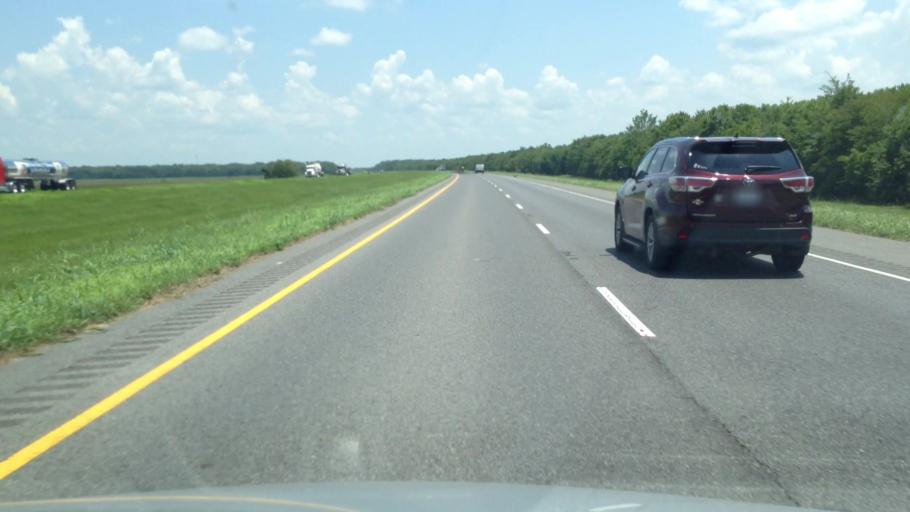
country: US
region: Louisiana
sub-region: Evangeline Parish
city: Ville Platte
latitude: 30.8086
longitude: -92.2162
